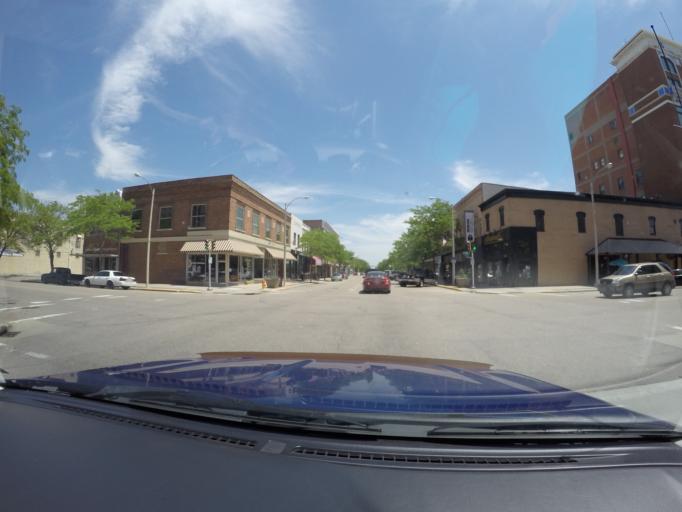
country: US
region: Nebraska
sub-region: Hall County
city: Grand Island
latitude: 40.9253
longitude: -98.3412
